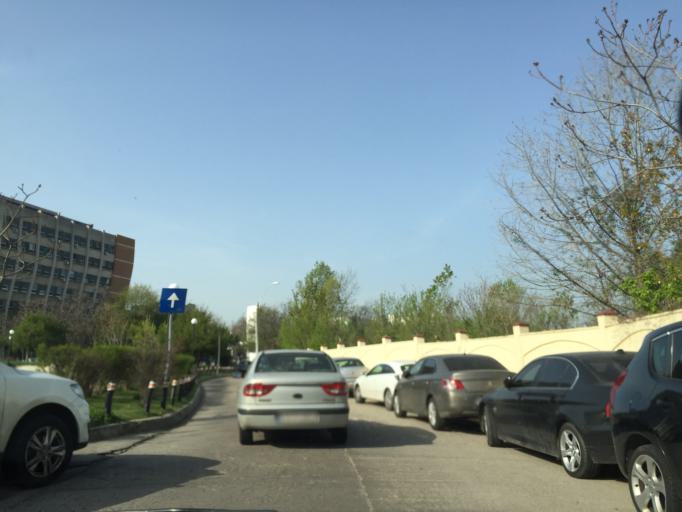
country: RO
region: Bucuresti
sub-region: Municipiul Bucuresti
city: Bucuresti
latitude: 44.4267
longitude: 26.0754
